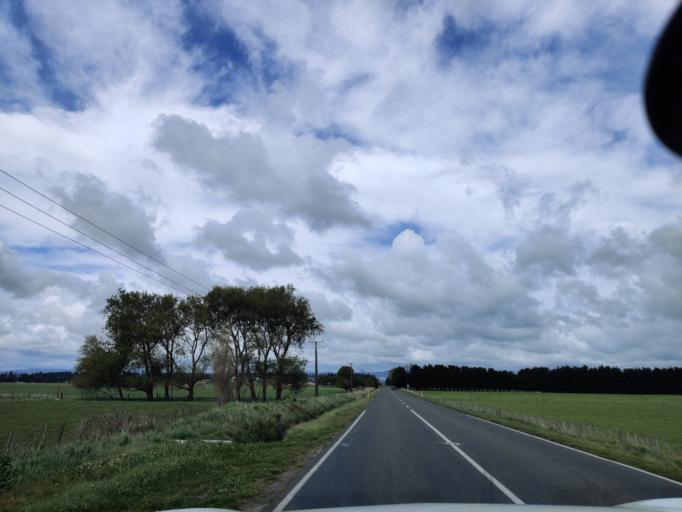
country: NZ
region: Manawatu-Wanganui
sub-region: Palmerston North City
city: Palmerston North
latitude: -40.3346
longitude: 175.5160
